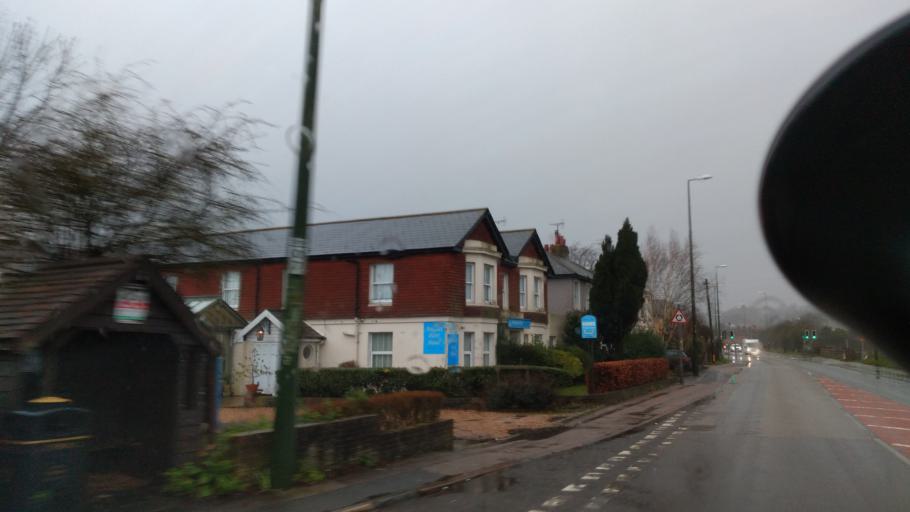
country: GB
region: England
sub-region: West Sussex
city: Arundel
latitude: 50.8492
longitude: -0.5471
